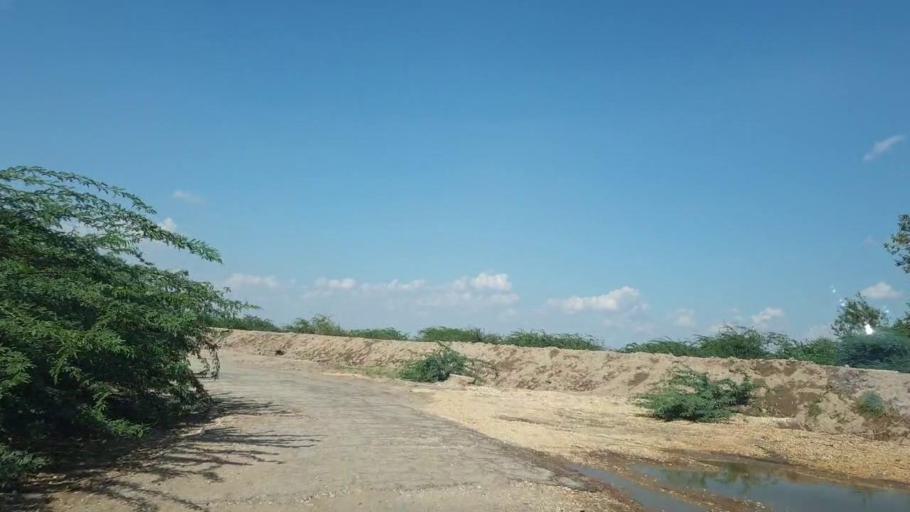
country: PK
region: Sindh
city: Pithoro
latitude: 25.6257
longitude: 69.4312
